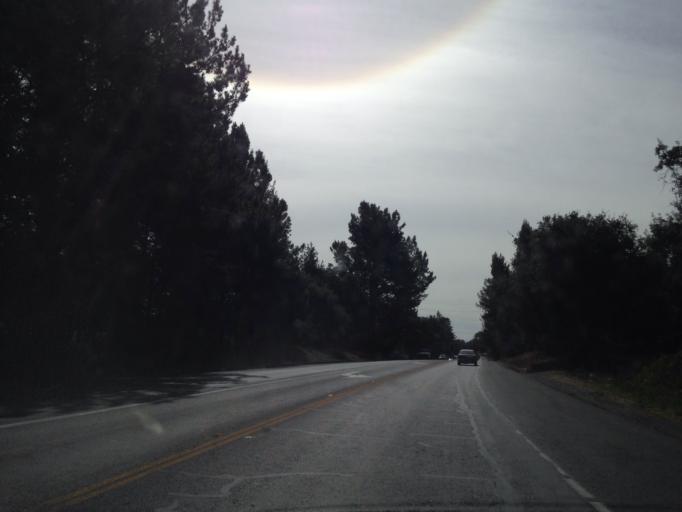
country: US
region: California
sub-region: Sonoma County
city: Graton
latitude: 38.4368
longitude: -122.8577
